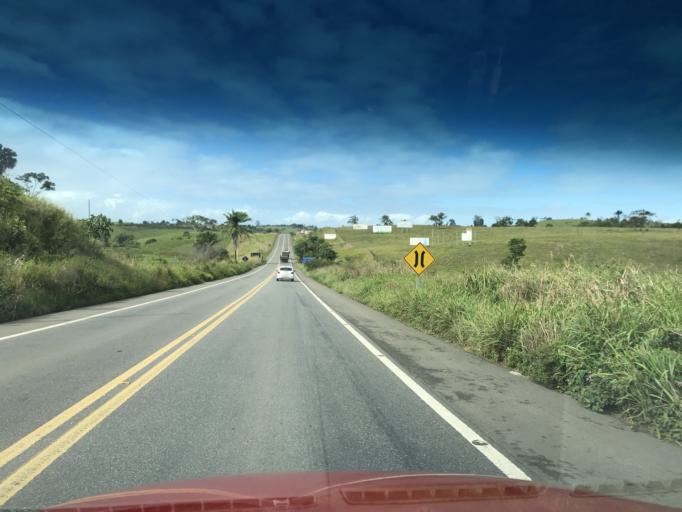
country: BR
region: Bahia
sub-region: Conceicao Do Almeida
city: Muritiba
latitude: -12.9329
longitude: -39.2535
